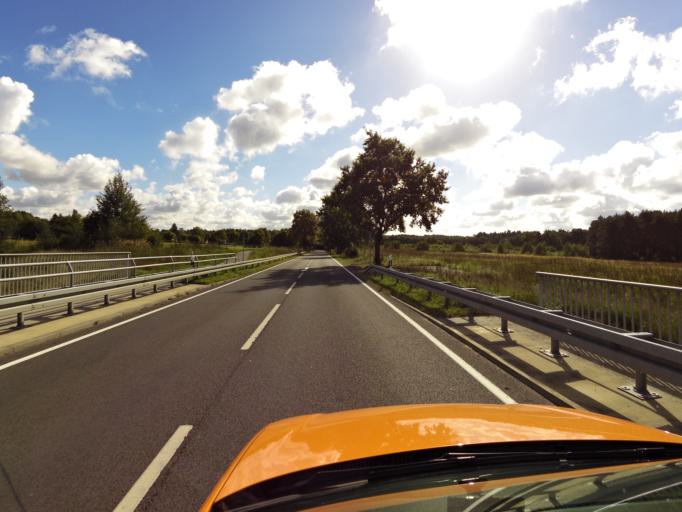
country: DE
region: Brandenburg
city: Michendorf
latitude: 52.3013
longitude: 13.0353
